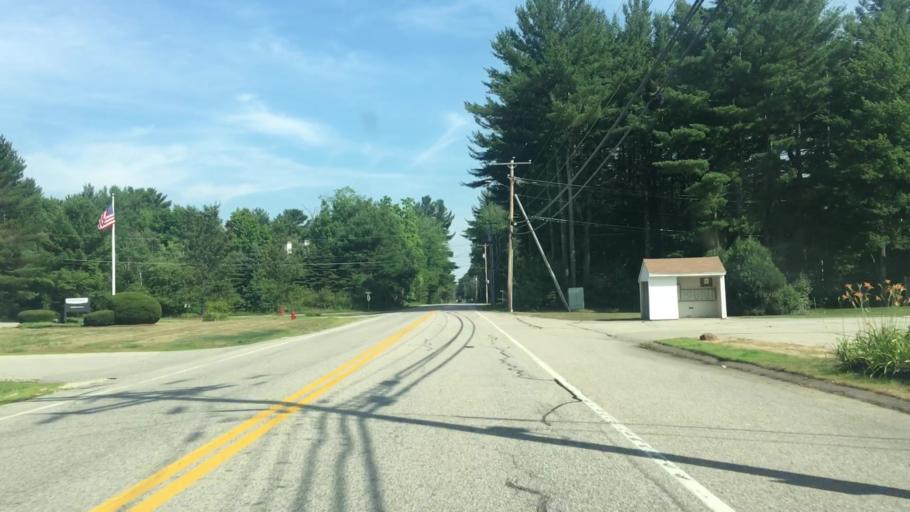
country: US
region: New Hampshire
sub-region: Strafford County
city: Rochester
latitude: 43.2817
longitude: -70.9718
